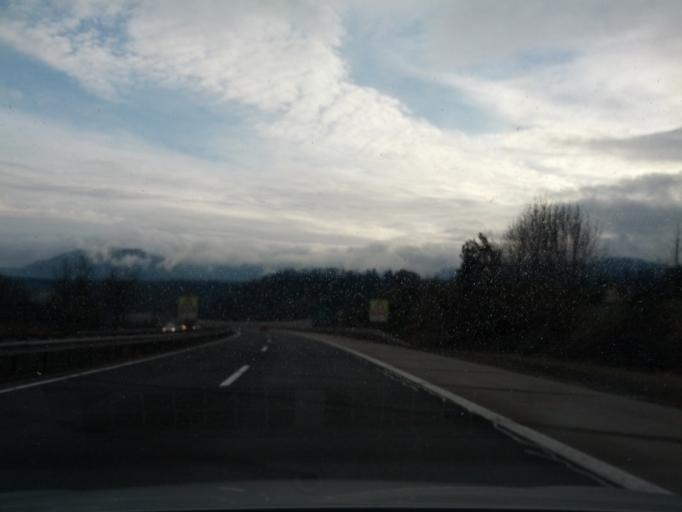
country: SI
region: Naklo
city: Naklo
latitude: 46.2968
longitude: 14.2839
